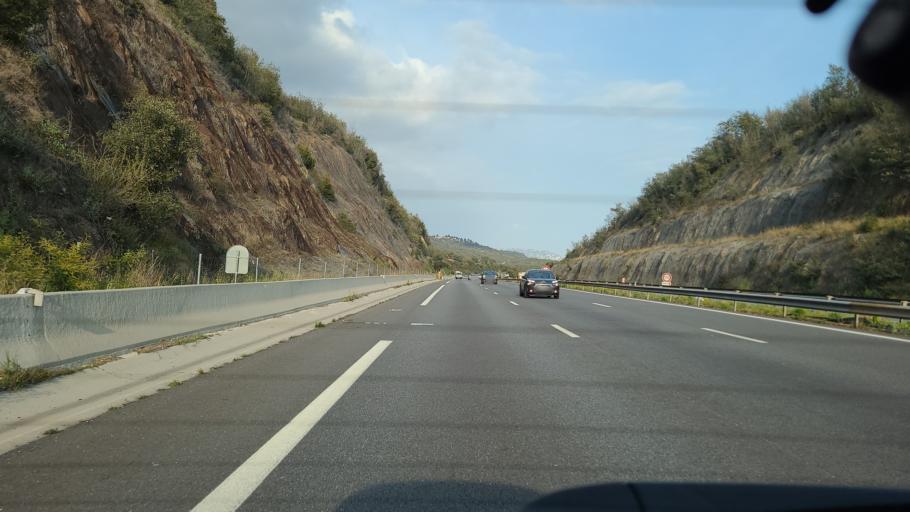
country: FR
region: Provence-Alpes-Cote d'Azur
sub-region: Departement du Var
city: Tanneron
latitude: 43.5340
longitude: 6.8787
